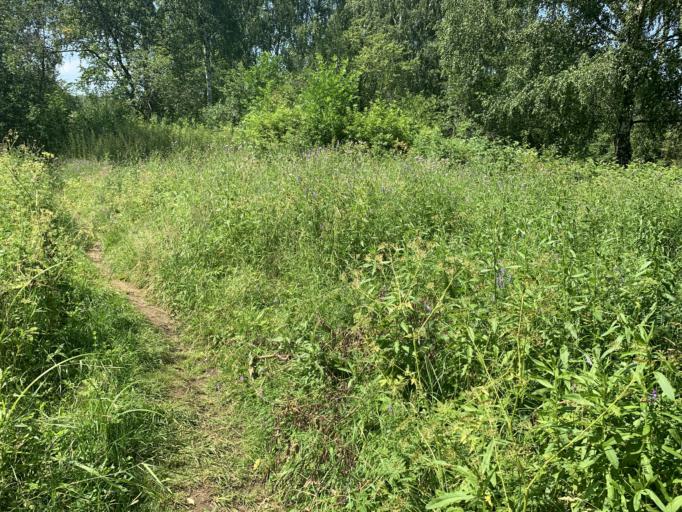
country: RU
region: Moskovskaya
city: Mamontovka
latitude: 55.9684
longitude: 37.8190
